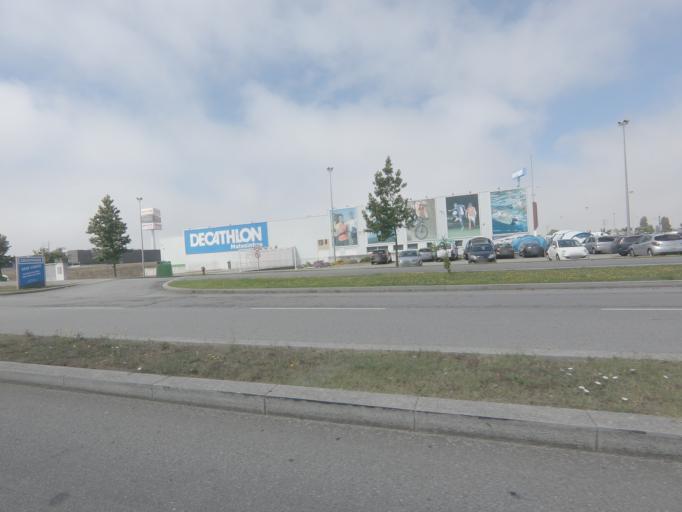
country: PT
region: Porto
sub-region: Matosinhos
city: Santa Cruz do Bispo
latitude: 41.2161
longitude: -8.6834
